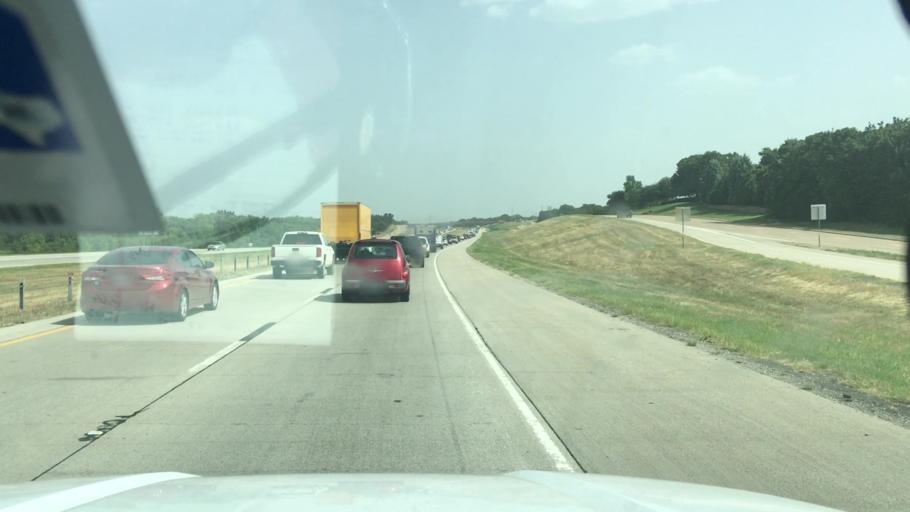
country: US
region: Texas
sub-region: Tarrant County
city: Grapevine
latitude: 32.8900
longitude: -97.0809
